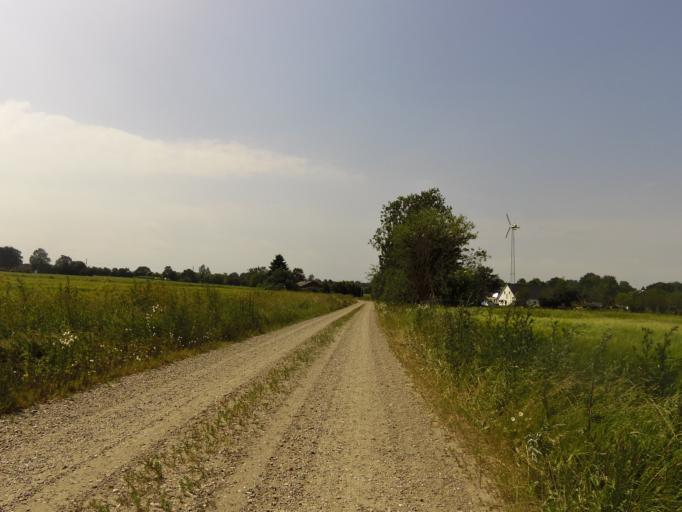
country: DK
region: South Denmark
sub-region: Aabenraa Kommune
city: Rodekro
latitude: 55.1416
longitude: 9.2107
